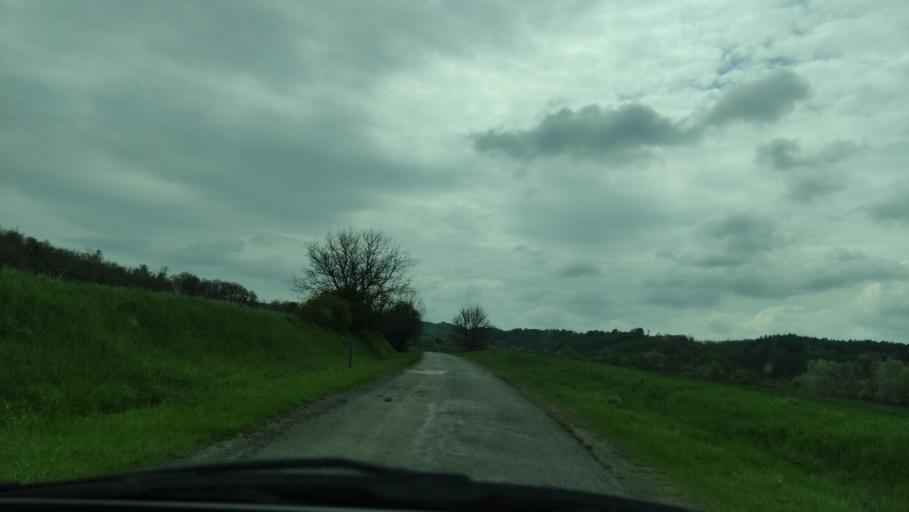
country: HU
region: Baranya
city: Magocs
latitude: 46.3032
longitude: 18.1922
